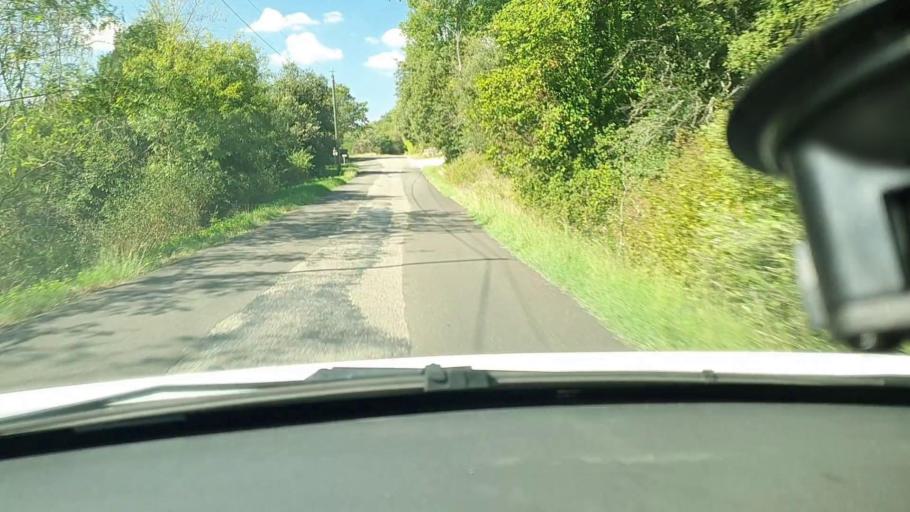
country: FR
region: Languedoc-Roussillon
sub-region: Departement du Gard
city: Goudargues
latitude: 44.1760
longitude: 4.4993
